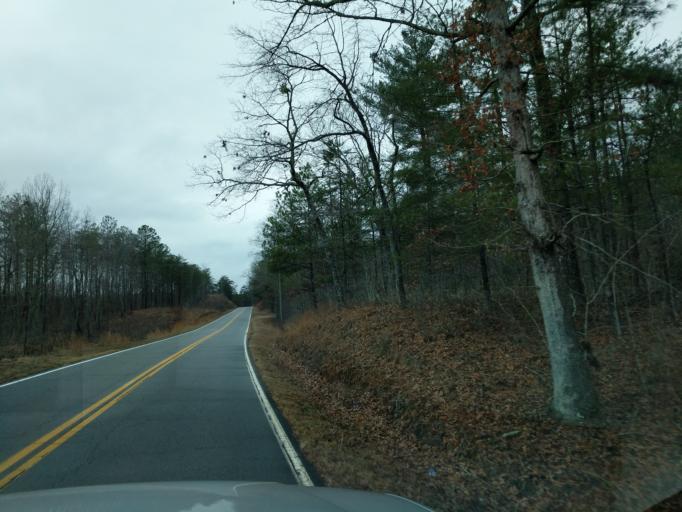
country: US
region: South Carolina
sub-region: Oconee County
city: Walhalla
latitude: 34.8007
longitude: -83.1535
